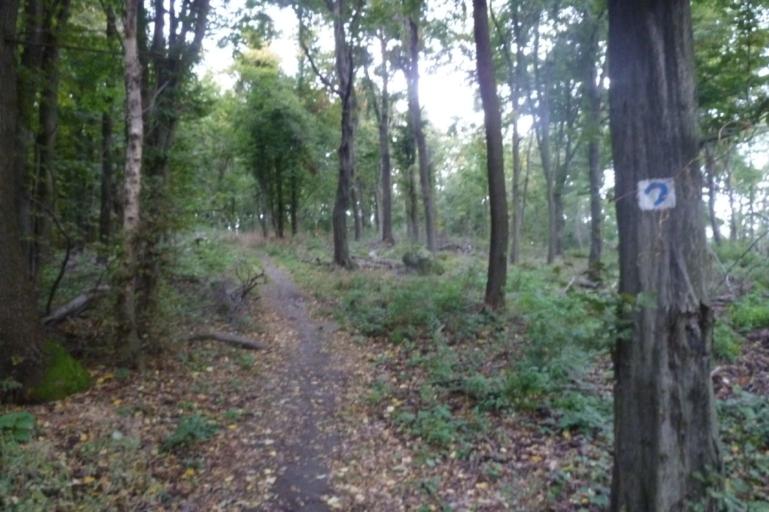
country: HU
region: Pest
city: Pilisszentkereszt
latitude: 47.7153
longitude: 18.9115
